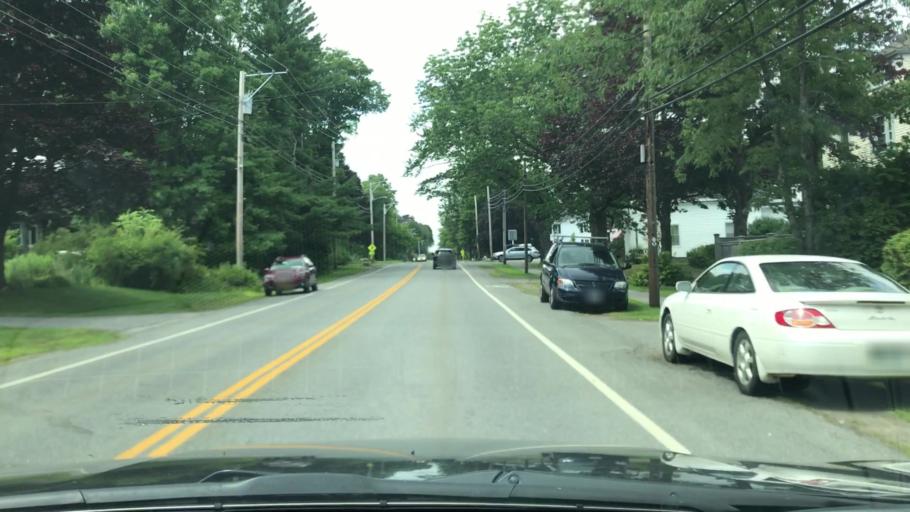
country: US
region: Maine
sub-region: Waldo County
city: Belfast
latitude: 44.4172
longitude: -68.9977
